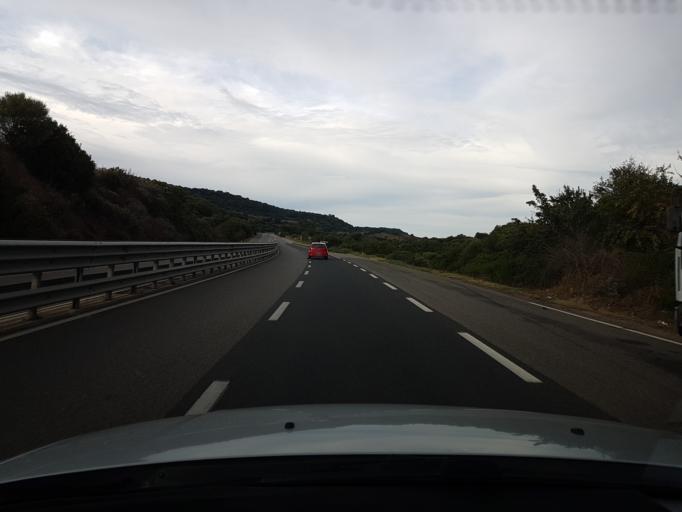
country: IT
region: Sardinia
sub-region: Provincia di Oristano
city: Sedilo
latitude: 40.1522
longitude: 8.9015
